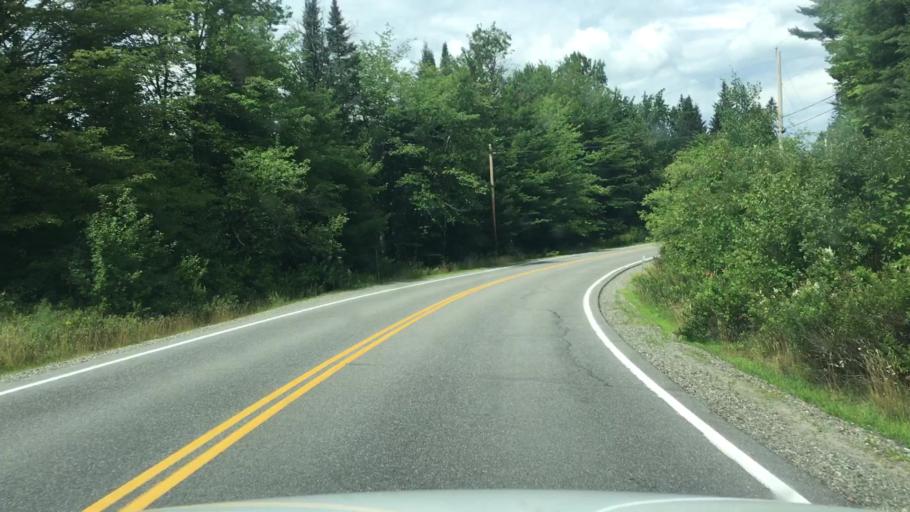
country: US
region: New Hampshire
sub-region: Grafton County
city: Deerfield
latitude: 44.2973
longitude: -71.6596
